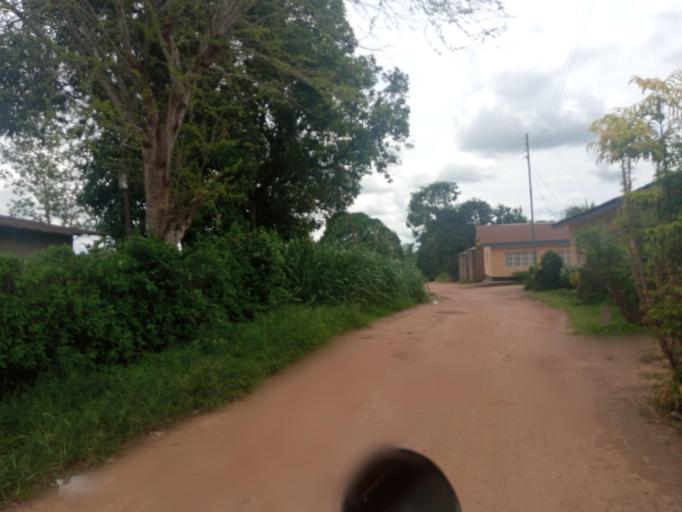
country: SL
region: Southern Province
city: Bo
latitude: 7.9565
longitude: -11.7171
